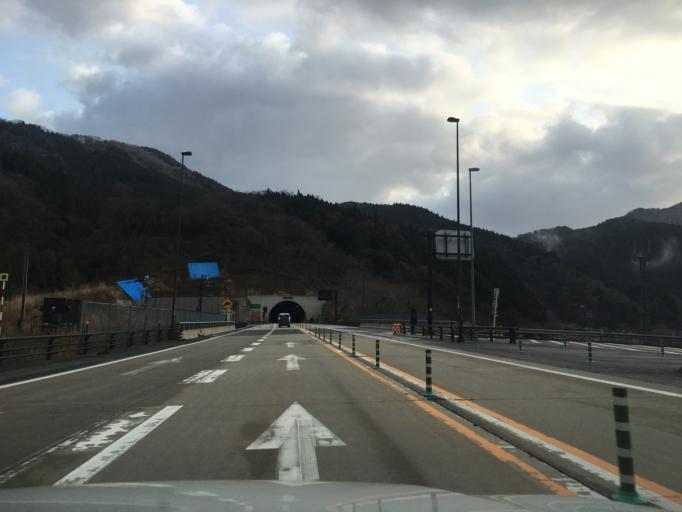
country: JP
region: Yamagata
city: Tsuruoka
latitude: 38.6669
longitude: 139.6243
